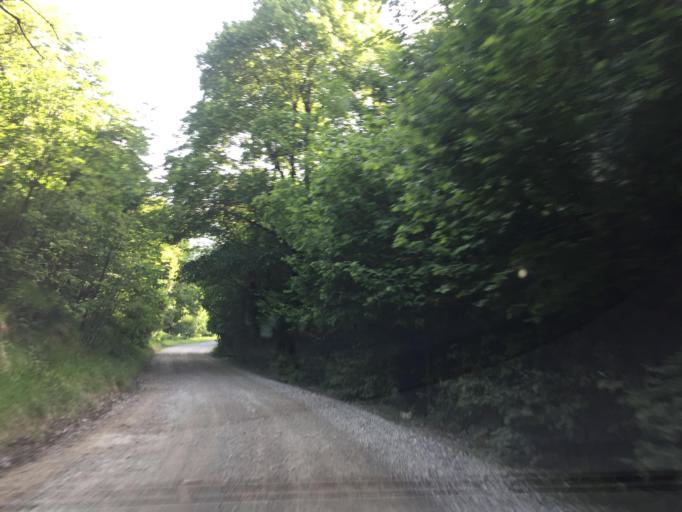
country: HR
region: Primorsko-Goranska
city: Klana
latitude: 45.4709
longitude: 14.4122
